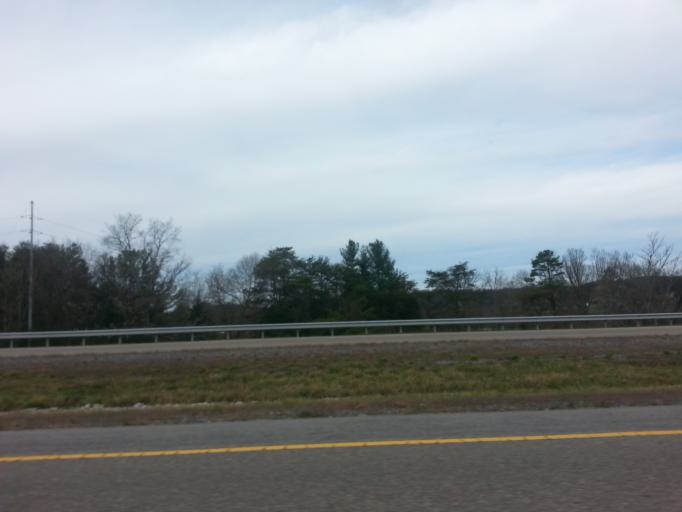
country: US
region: Tennessee
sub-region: Cocke County
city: Newport
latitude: 36.0032
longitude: -83.0949
